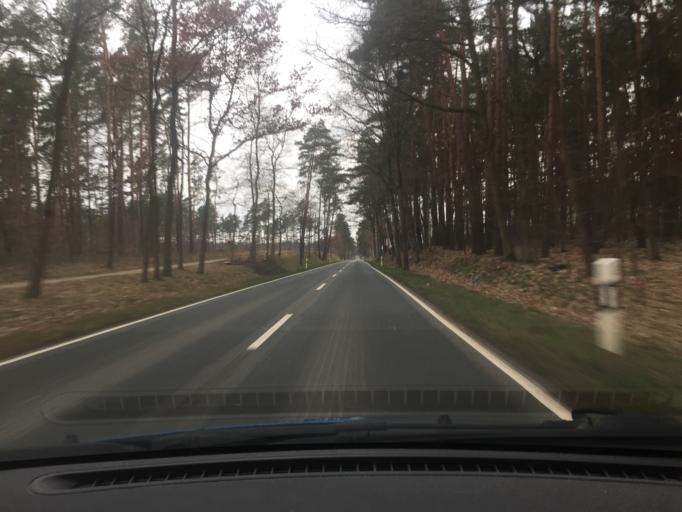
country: DE
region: Lower Saxony
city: Rosche
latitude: 52.9897
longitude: 10.7350
